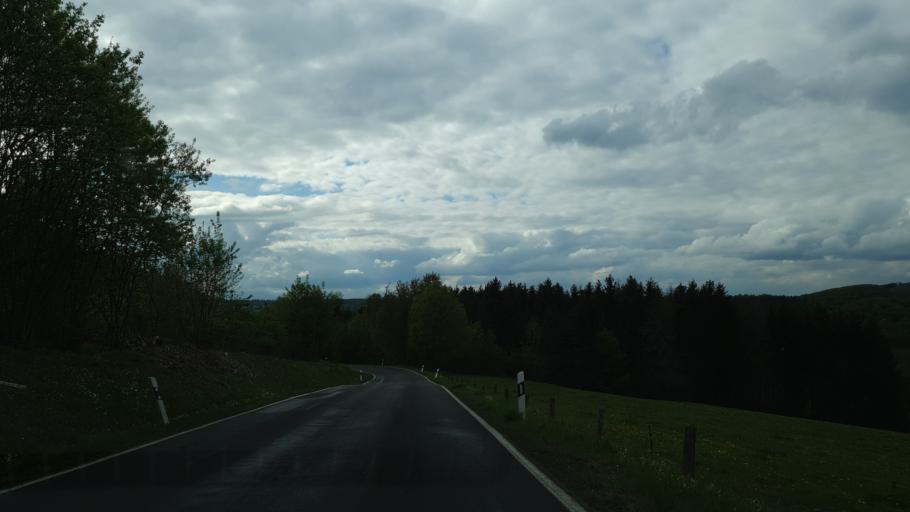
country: DE
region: Rheinland-Pfalz
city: Dreisbach
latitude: 50.6198
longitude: 7.9252
